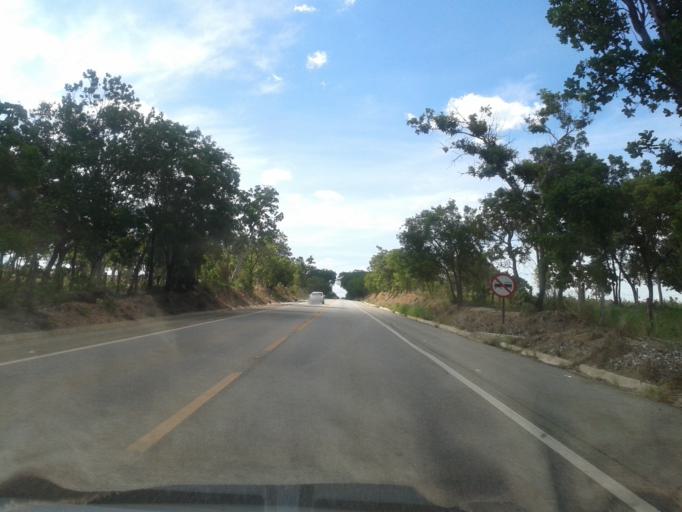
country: BR
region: Goias
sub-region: Itapuranga
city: Itapuranga
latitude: -15.4730
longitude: -50.3425
